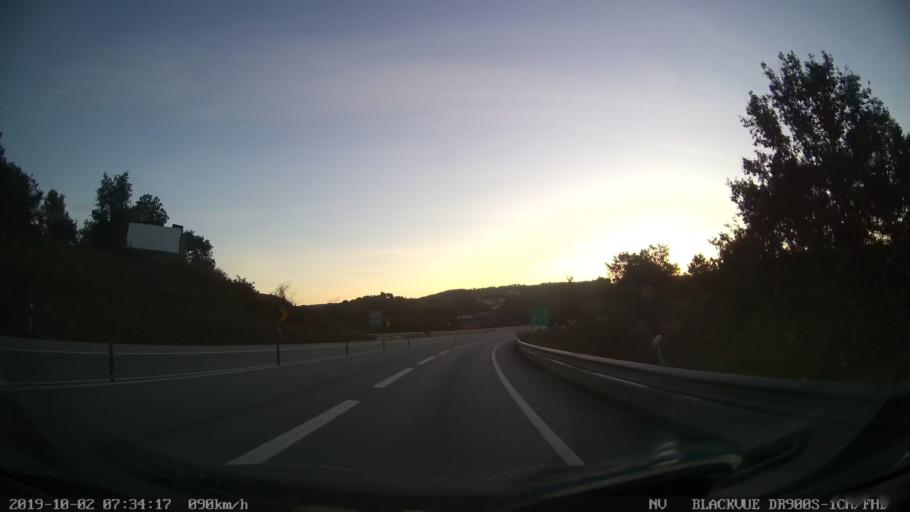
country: PT
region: Vila Real
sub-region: Vila Real
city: Vila Real
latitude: 41.3153
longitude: -7.7248
